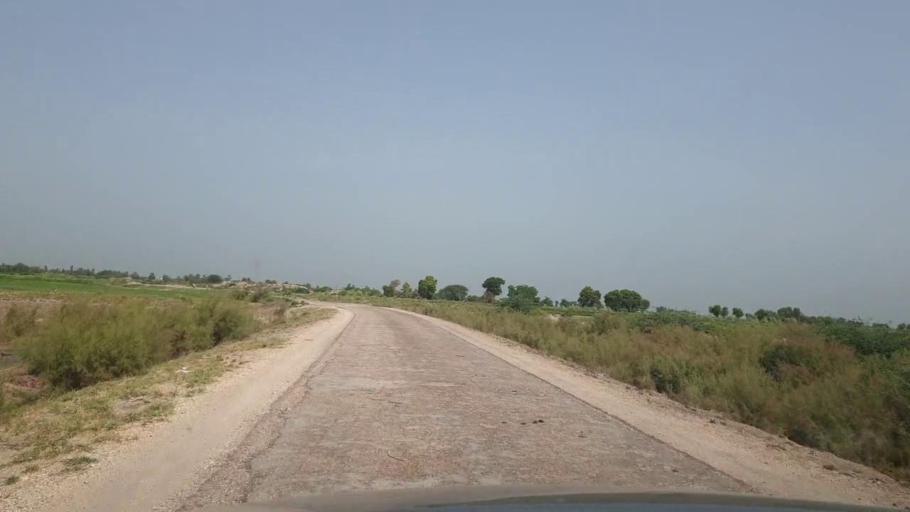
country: PK
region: Sindh
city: Madeji
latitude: 27.8392
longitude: 68.4417
